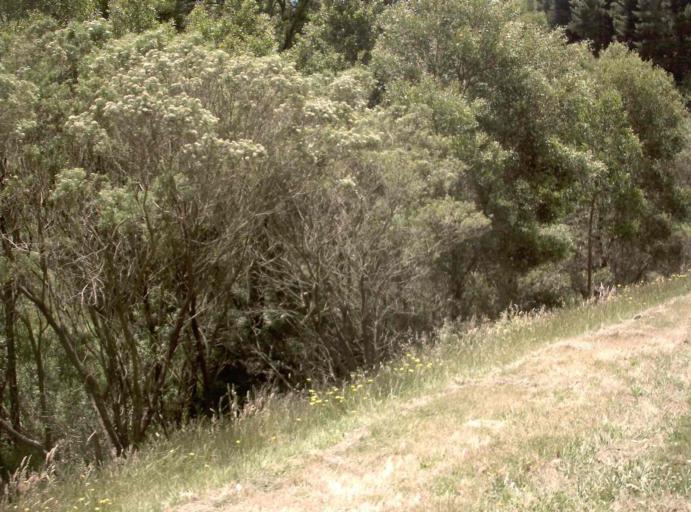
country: AU
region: Victoria
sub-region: Bass Coast
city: North Wonthaggi
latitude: -38.7175
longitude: 146.1167
